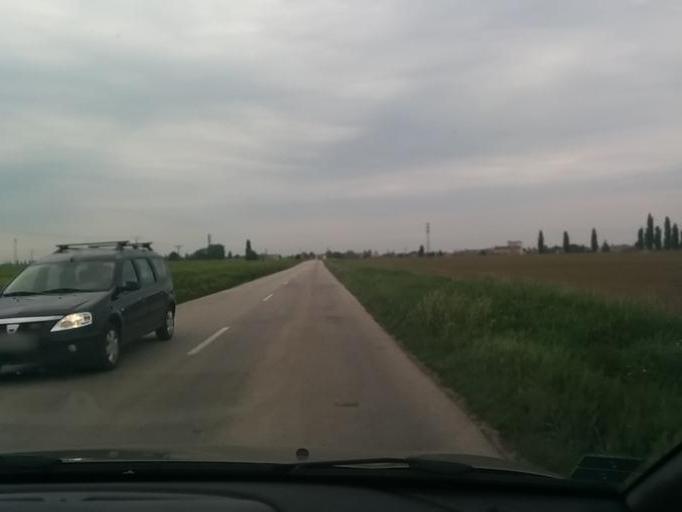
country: SK
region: Trnavsky
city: Sladkovicovo
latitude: 48.2084
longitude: 17.6214
